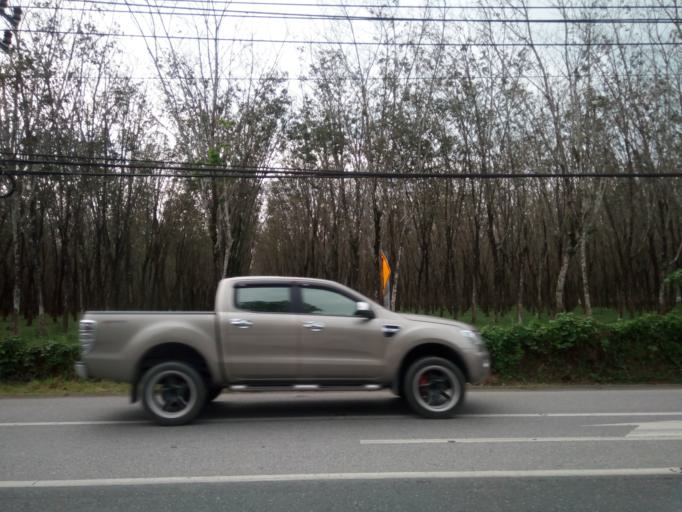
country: TH
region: Phuket
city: Thalang
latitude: 8.0500
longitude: 98.3379
